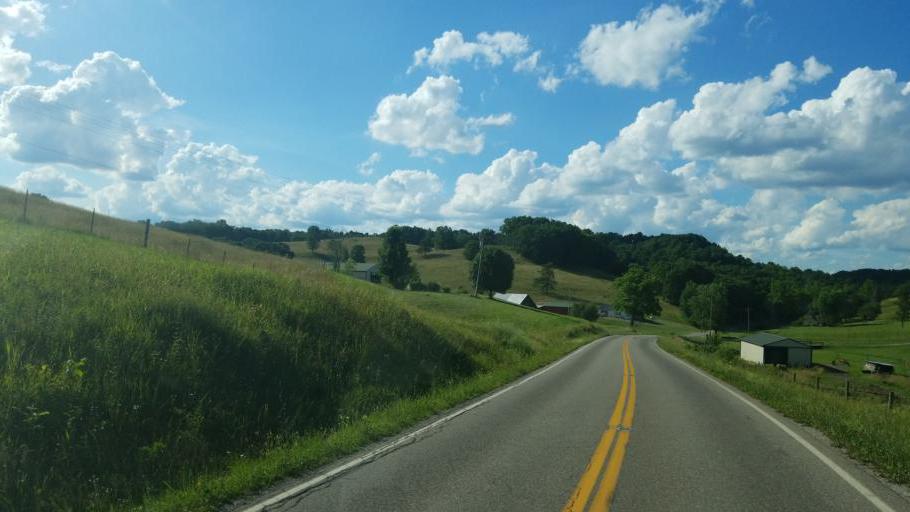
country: US
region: Ohio
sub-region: Gallia County
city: Gallipolis
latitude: 38.7620
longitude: -82.3553
